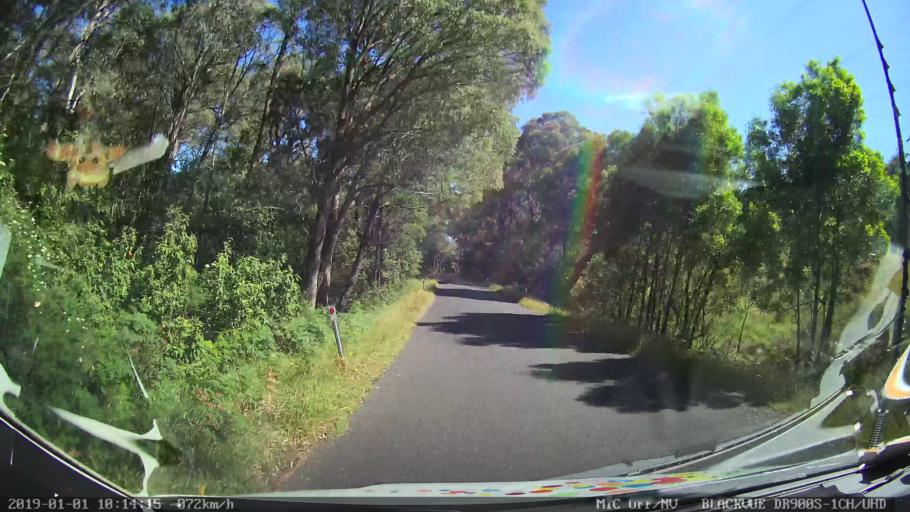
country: AU
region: New South Wales
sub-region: Snowy River
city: Jindabyne
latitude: -36.1142
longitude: 148.1610
